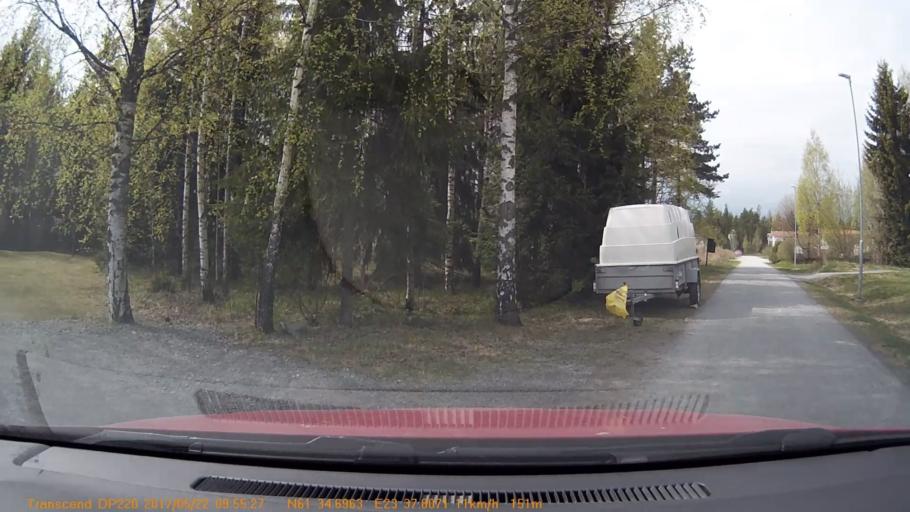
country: FI
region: Pirkanmaa
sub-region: Tampere
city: Yloejaervi
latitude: 61.5783
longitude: 23.6303
